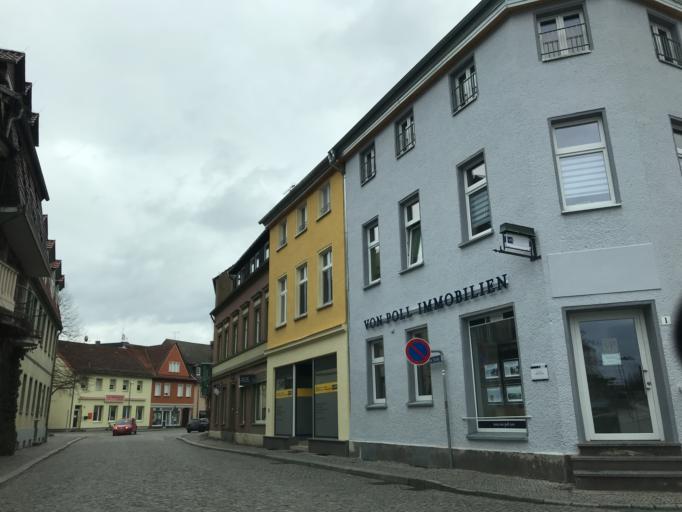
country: DE
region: Brandenburg
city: Luebben
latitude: 51.9417
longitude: 13.9011
